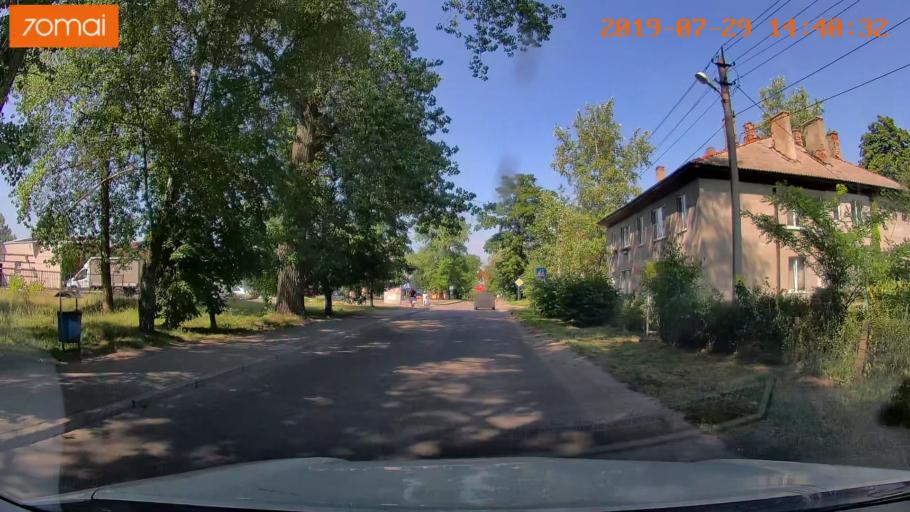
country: RU
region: Kaliningrad
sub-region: Gorod Kaliningrad
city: Baltiysk
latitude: 54.6548
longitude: 19.9011
